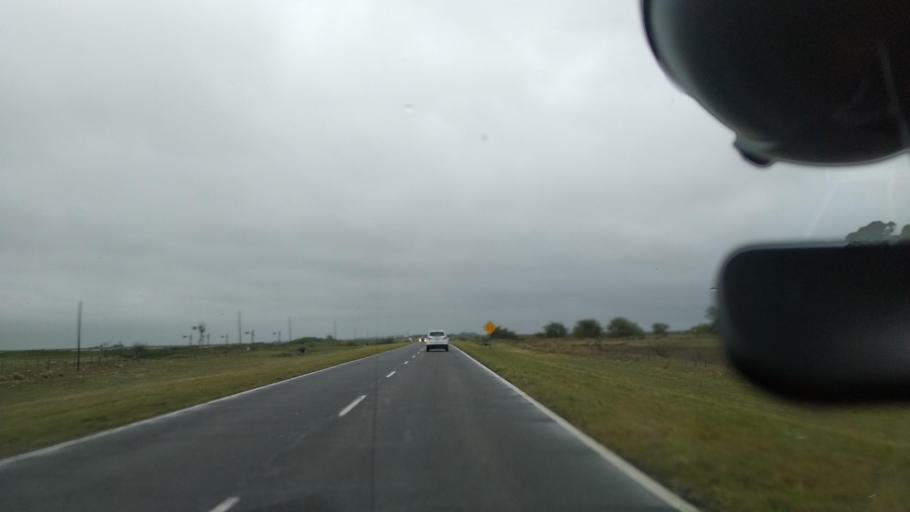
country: AR
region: Buenos Aires
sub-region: Partido de Dolores
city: Dolores
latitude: -36.0980
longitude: -57.4341
